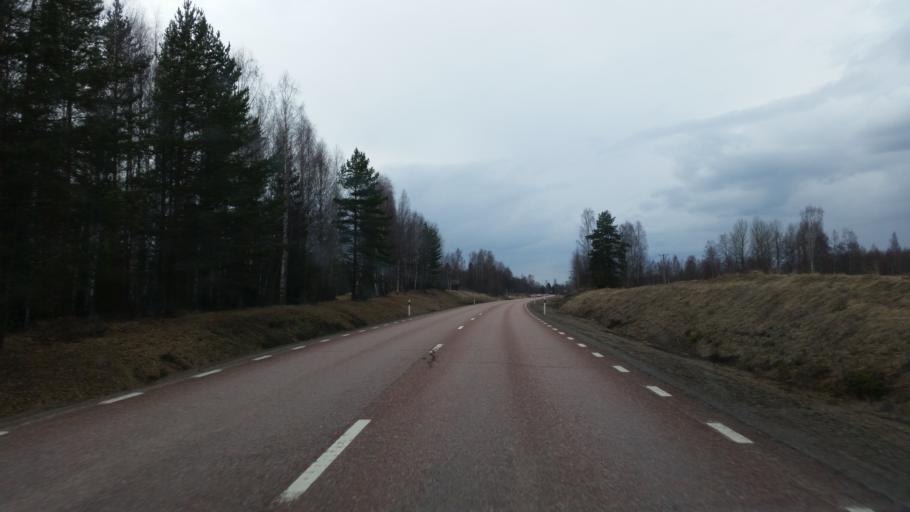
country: SE
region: Gaevleborg
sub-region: Ljusdals Kommun
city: Ljusdal
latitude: 61.8086
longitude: 16.0963
